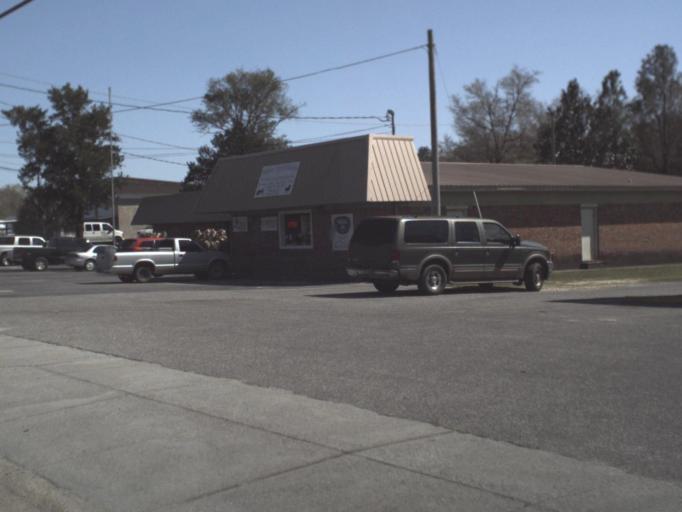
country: US
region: Florida
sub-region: Walton County
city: DeFuniak Springs
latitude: 30.7285
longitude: -86.1346
